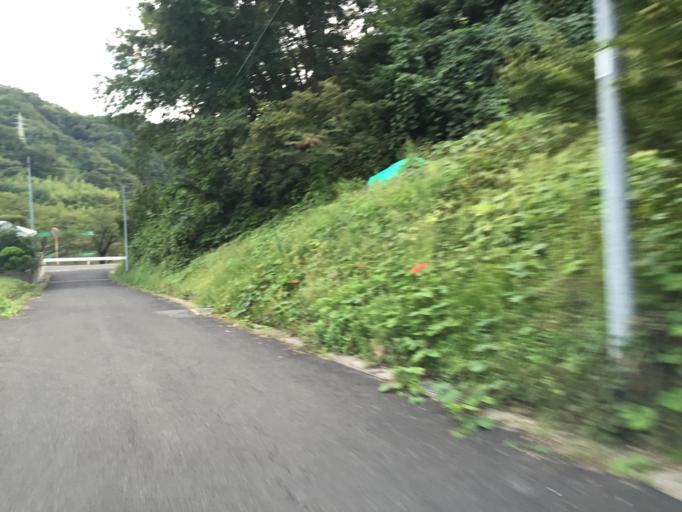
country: JP
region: Fukushima
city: Fukushima-shi
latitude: 37.7502
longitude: 140.4994
